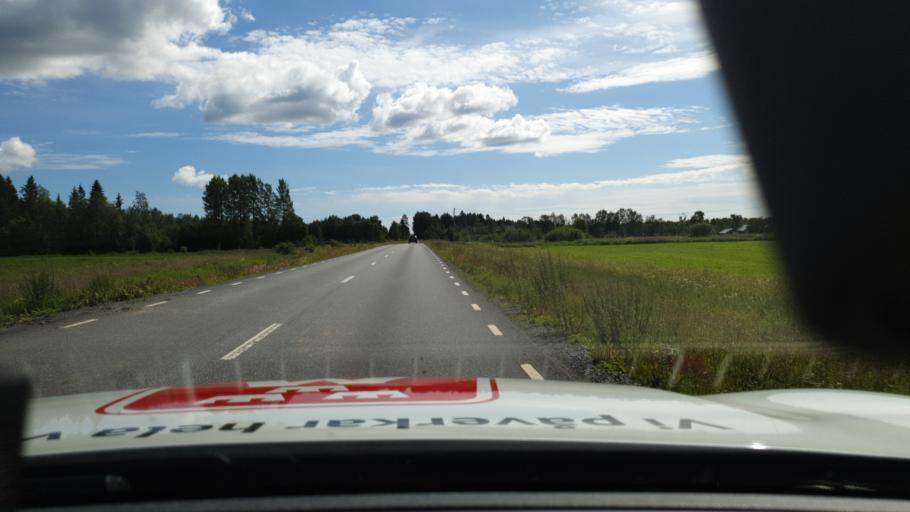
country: SE
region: Norrbotten
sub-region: Lulea Kommun
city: Gammelstad
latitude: 65.7959
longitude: 22.0691
